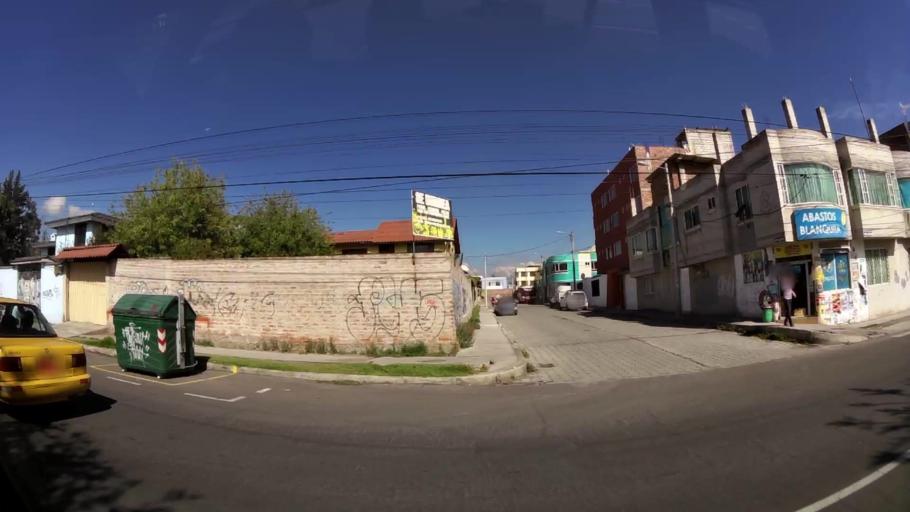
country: EC
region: Chimborazo
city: Riobamba
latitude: -1.6594
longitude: -78.6734
